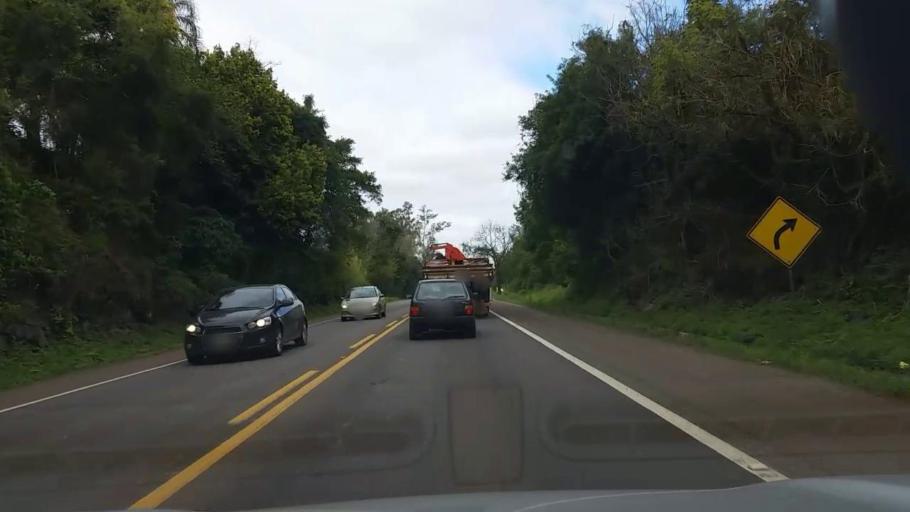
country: BR
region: Rio Grande do Sul
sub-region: Lajeado
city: Lajeado
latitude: -29.4198
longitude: -52.0230
